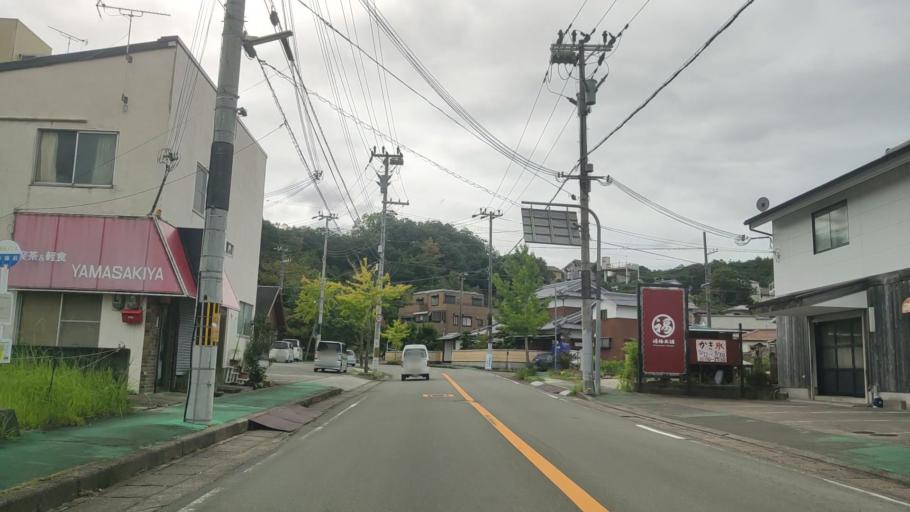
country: JP
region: Wakayama
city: Tanabe
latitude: 33.6777
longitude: 135.3741
